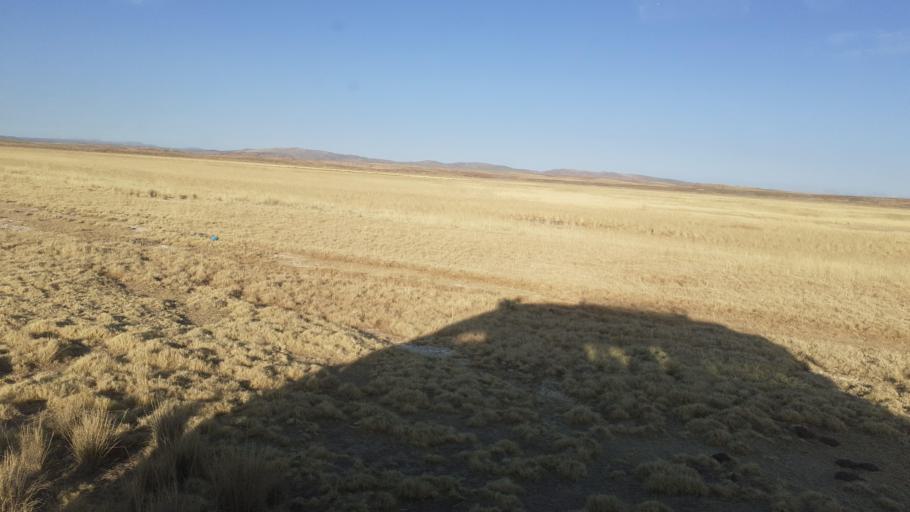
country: BO
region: La Paz
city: Tiahuanaco
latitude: -16.9462
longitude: -68.7625
